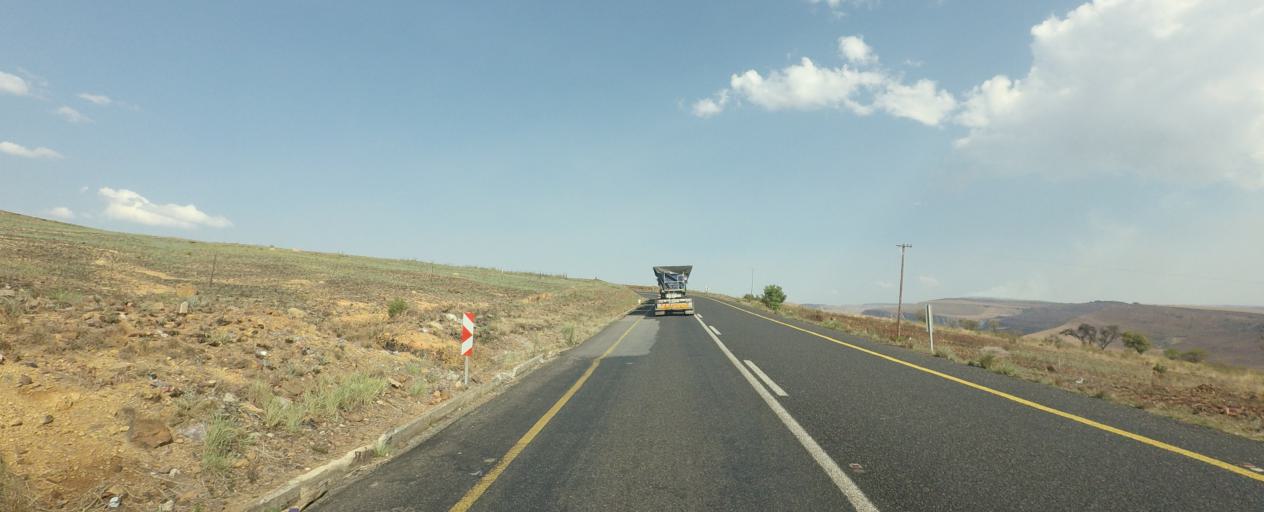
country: ZA
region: Mpumalanga
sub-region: Ehlanzeni District
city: Lydenburg
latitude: -25.1126
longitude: 30.5036
